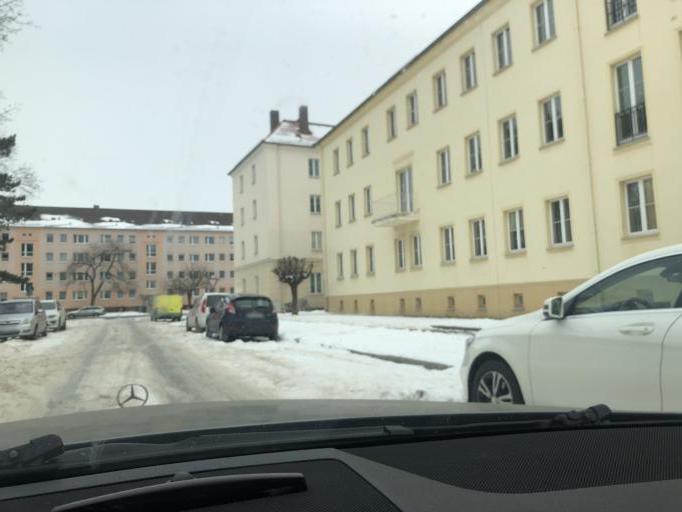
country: DE
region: Brandenburg
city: Guben
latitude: 51.9463
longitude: 14.7050
